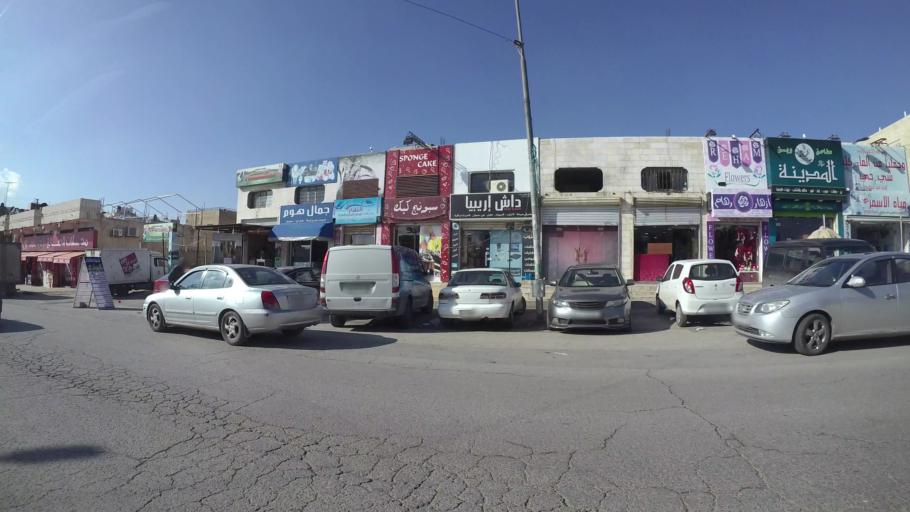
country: JO
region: Amman
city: Al Bunayyat ash Shamaliyah
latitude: 31.9028
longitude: 35.9135
